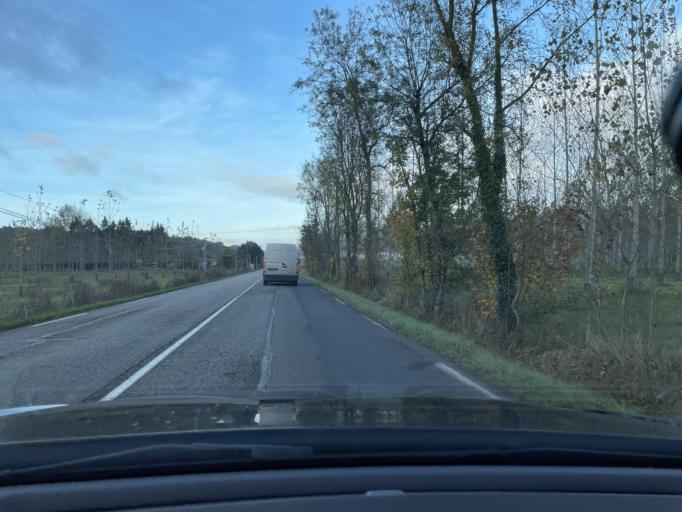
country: FR
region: Aquitaine
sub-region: Departement du Lot-et-Garonne
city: Casteljaloux
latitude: 44.3881
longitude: 0.1057
